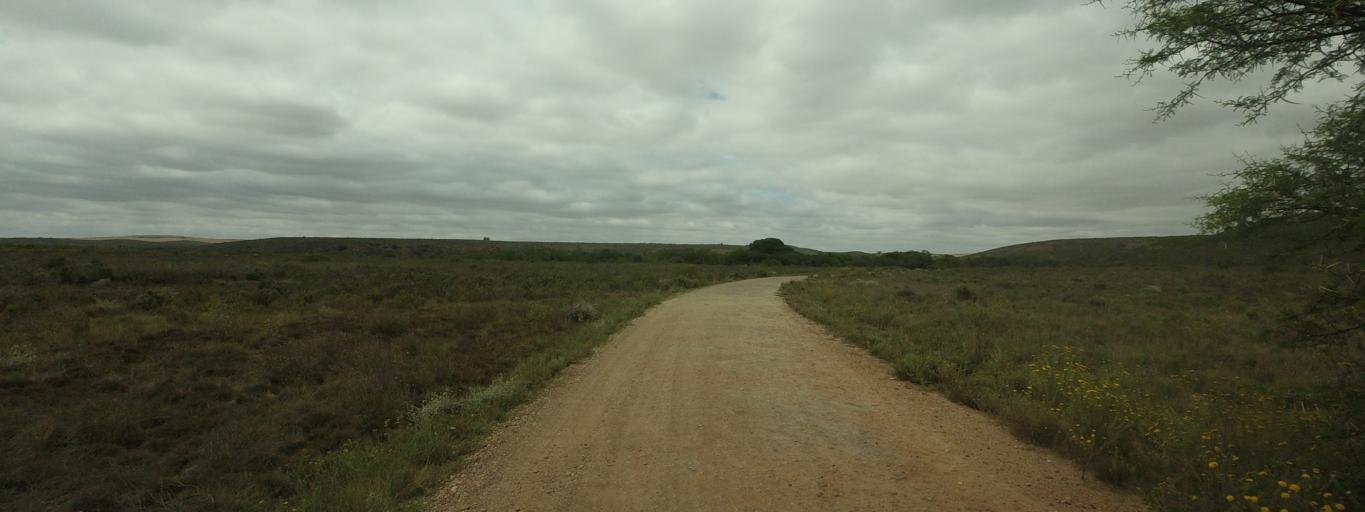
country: ZA
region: Western Cape
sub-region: Overberg District Municipality
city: Swellendam
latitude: -34.0643
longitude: 20.4388
